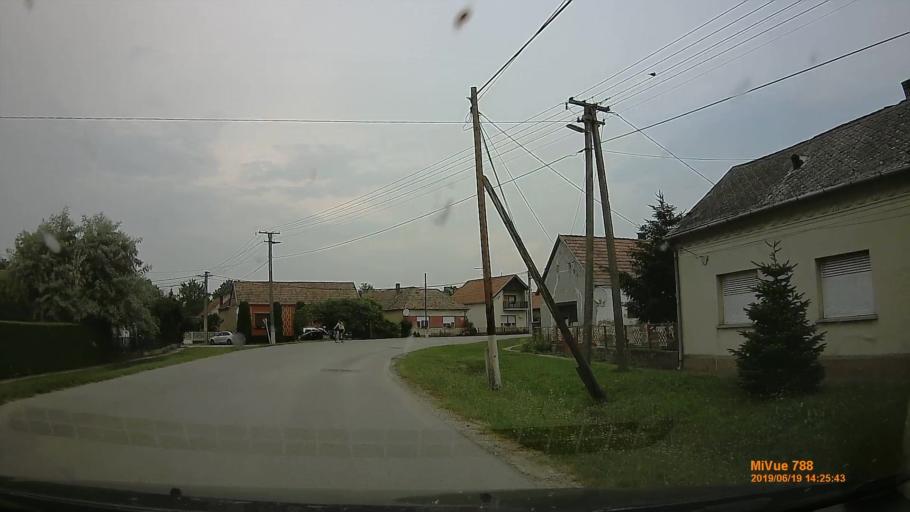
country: HU
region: Baranya
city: Szigetvar
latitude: 46.0255
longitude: 17.7774
